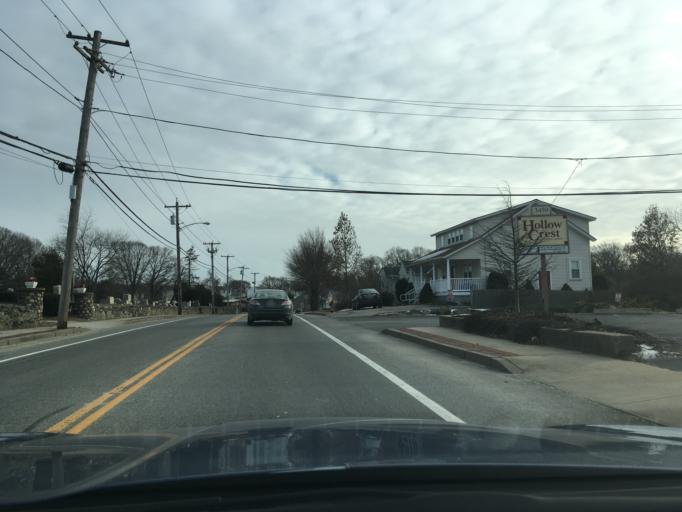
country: US
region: Rhode Island
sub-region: Kent County
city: East Greenwich
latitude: 41.6952
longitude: -71.4579
